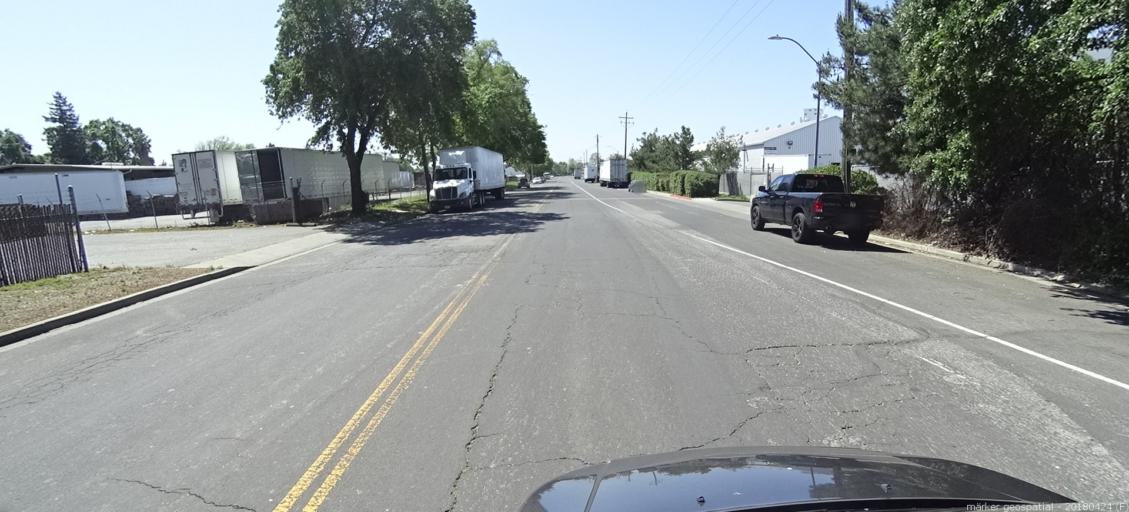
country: US
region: California
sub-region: Yolo County
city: West Sacramento
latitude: 38.5681
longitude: -121.5387
